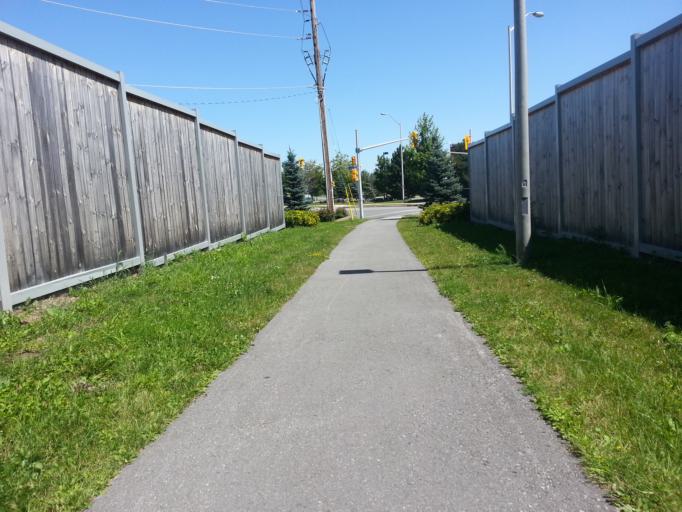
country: CA
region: Ontario
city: Bells Corners
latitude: 45.3219
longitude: -75.9267
